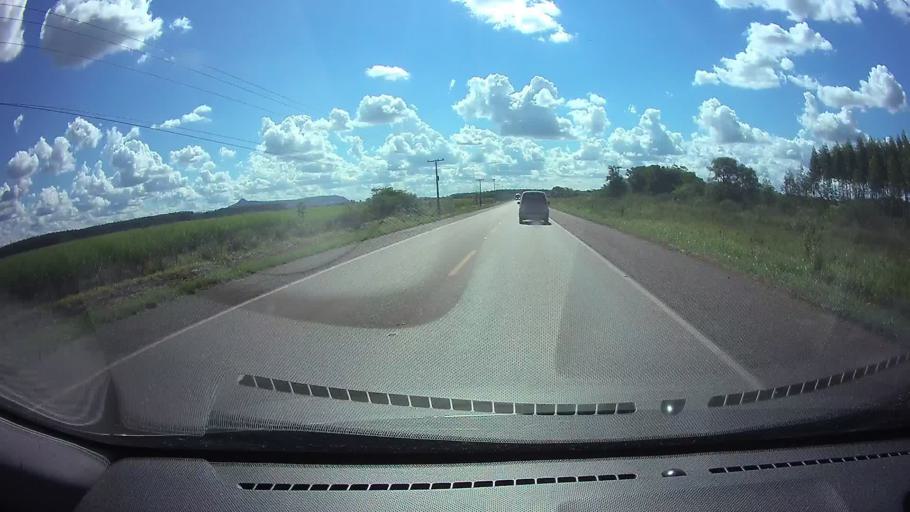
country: PY
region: Guaira
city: Coronel Martinez
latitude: -25.7629
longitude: -56.6877
